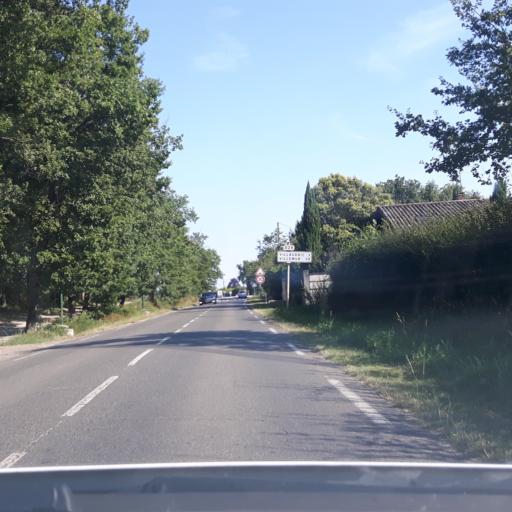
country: FR
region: Midi-Pyrenees
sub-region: Departement de la Haute-Garonne
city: Fronton
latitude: 43.8374
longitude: 1.3945
